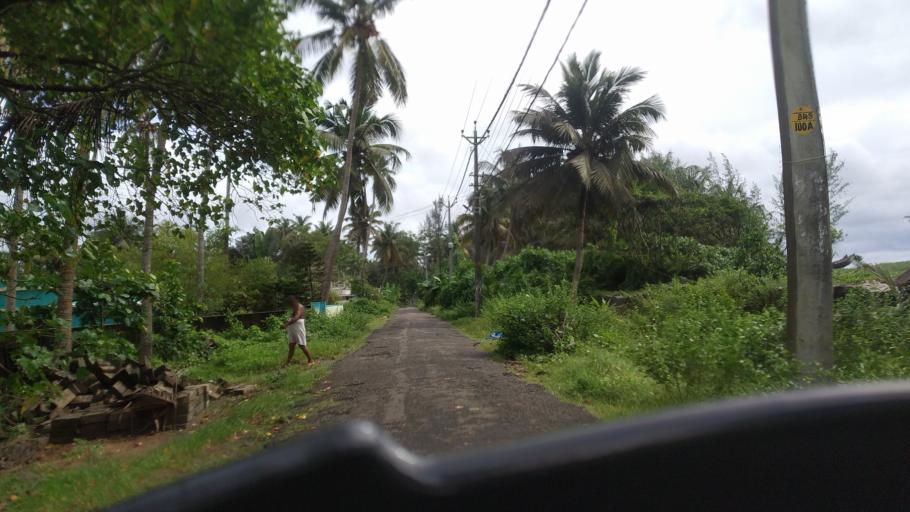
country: IN
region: Kerala
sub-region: Thrissur District
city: Kodungallur
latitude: 10.1154
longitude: 76.1864
